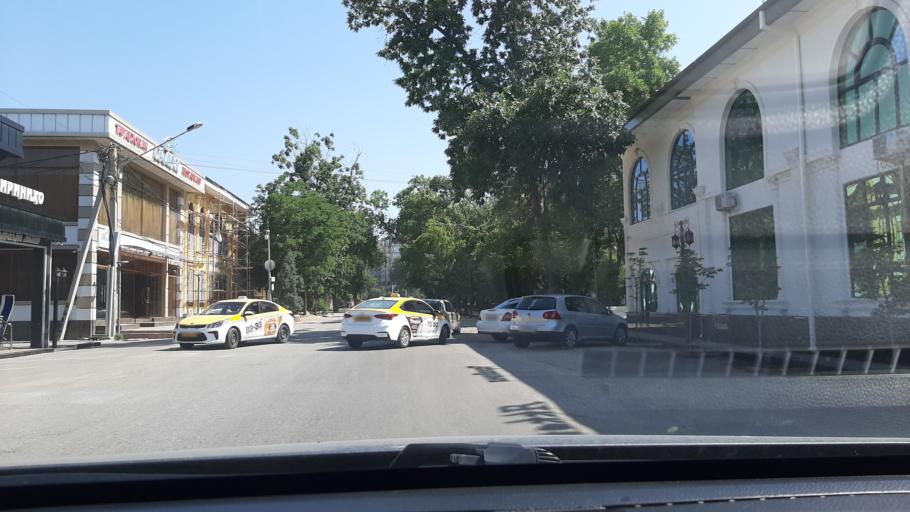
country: TJ
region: Dushanbe
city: Dushanbe
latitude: 38.5564
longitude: 68.7569
